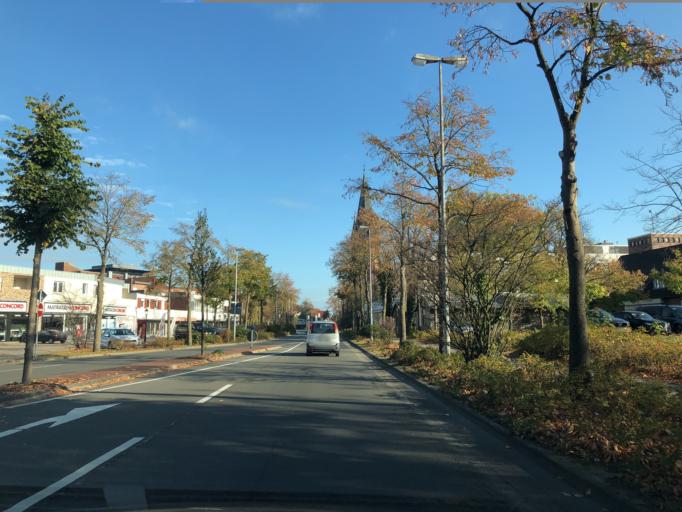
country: DE
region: Lower Saxony
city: Papenburg
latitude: 53.0773
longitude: 7.3924
